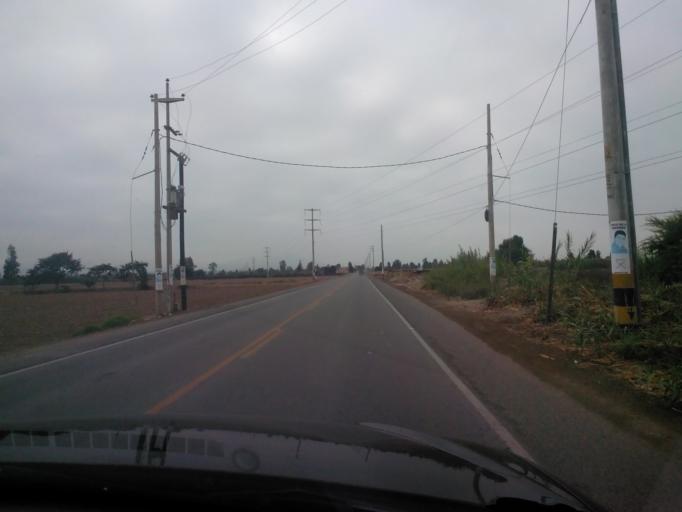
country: PE
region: Ica
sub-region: Provincia de Pisco
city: Independencia
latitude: -13.6803
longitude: -76.0730
